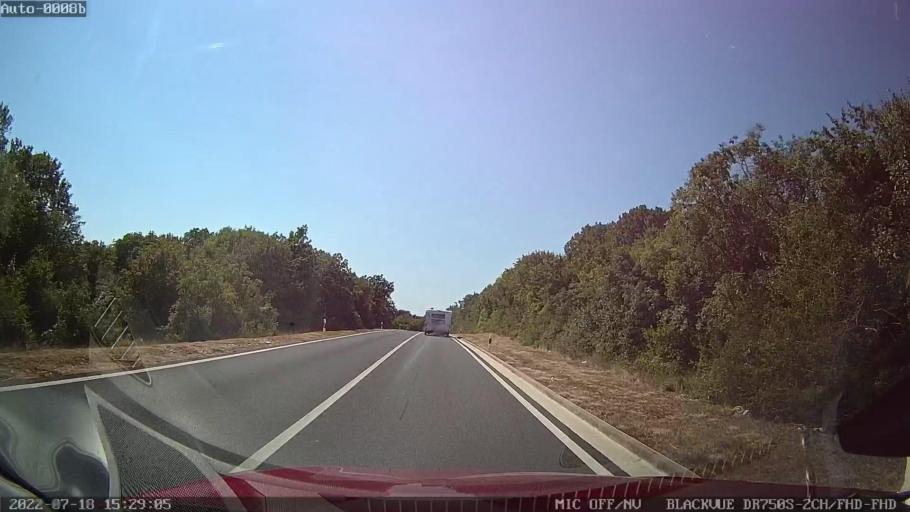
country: HR
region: Istarska
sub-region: Grad Rovinj
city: Rovinj
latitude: 45.1089
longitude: 13.7775
